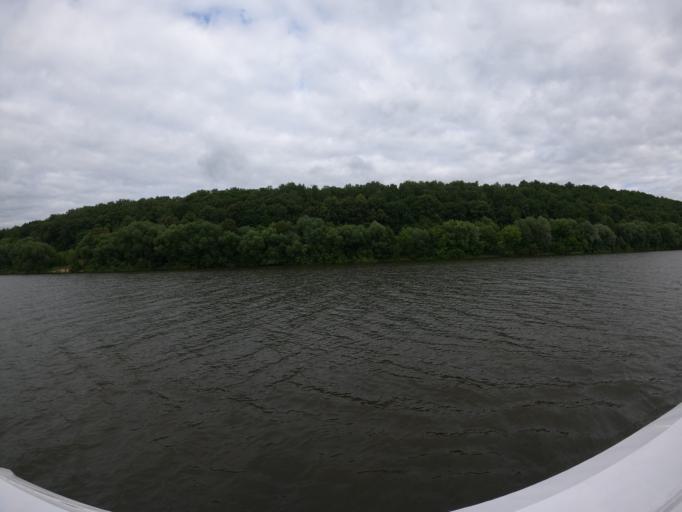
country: RU
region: Moskovskaya
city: Sychevo
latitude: 54.9567
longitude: 38.7699
